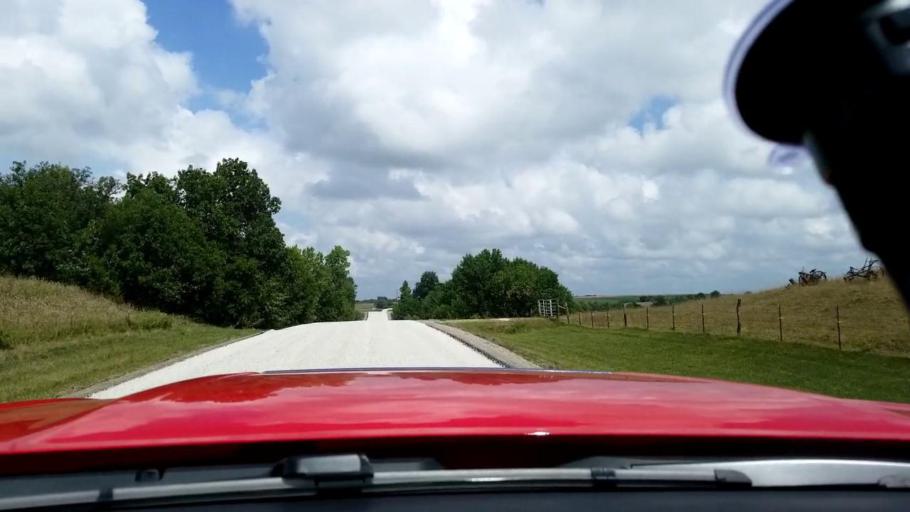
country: US
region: Iowa
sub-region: Decatur County
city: Lamoni
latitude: 40.6432
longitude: -94.0530
